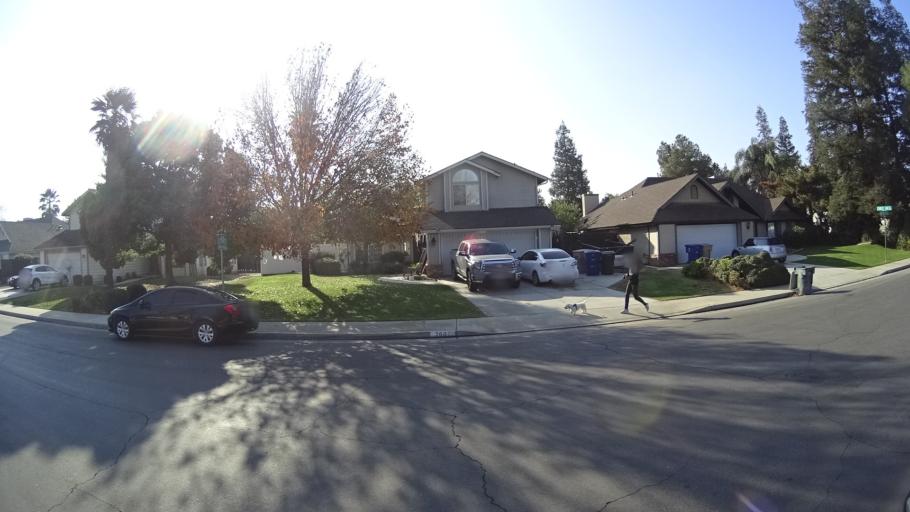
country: US
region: California
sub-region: Kern County
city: Greenacres
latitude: 35.3321
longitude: -119.1070
